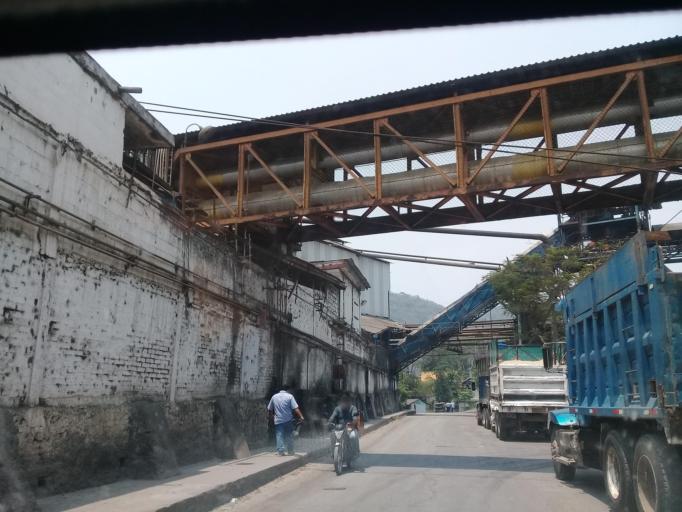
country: MX
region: Veracruz
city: Tezonapa
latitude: 18.6049
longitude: -96.6859
